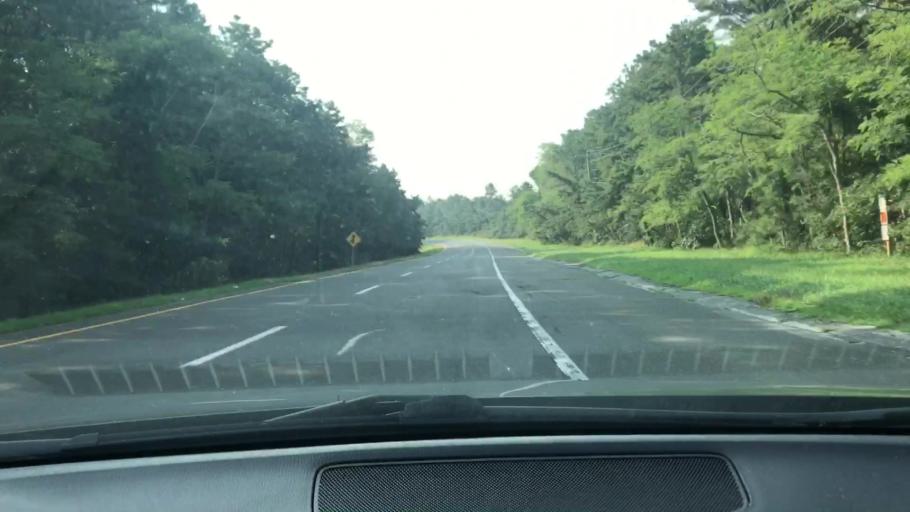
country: US
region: New York
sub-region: Suffolk County
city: Riverhead
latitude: 40.9004
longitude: -72.6512
